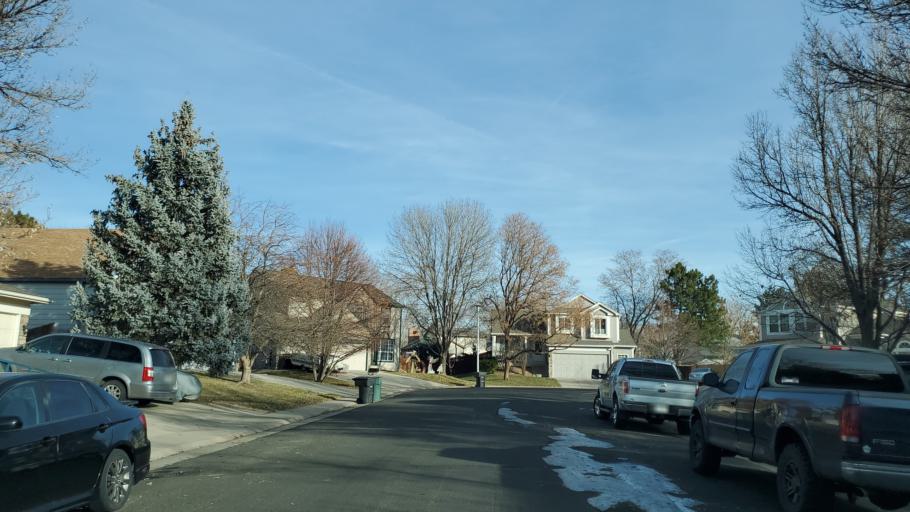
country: US
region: Colorado
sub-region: Adams County
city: Northglenn
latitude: 39.9046
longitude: -104.9525
